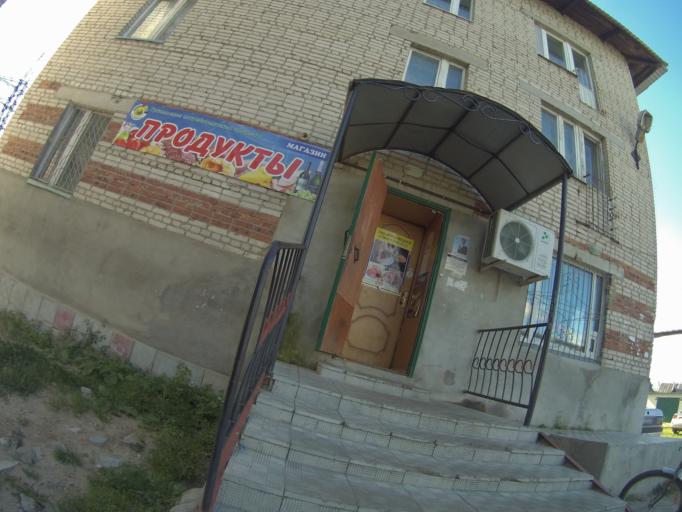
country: RU
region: Vladimir
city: Urshel'skiy
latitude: 55.6798
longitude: 40.2244
